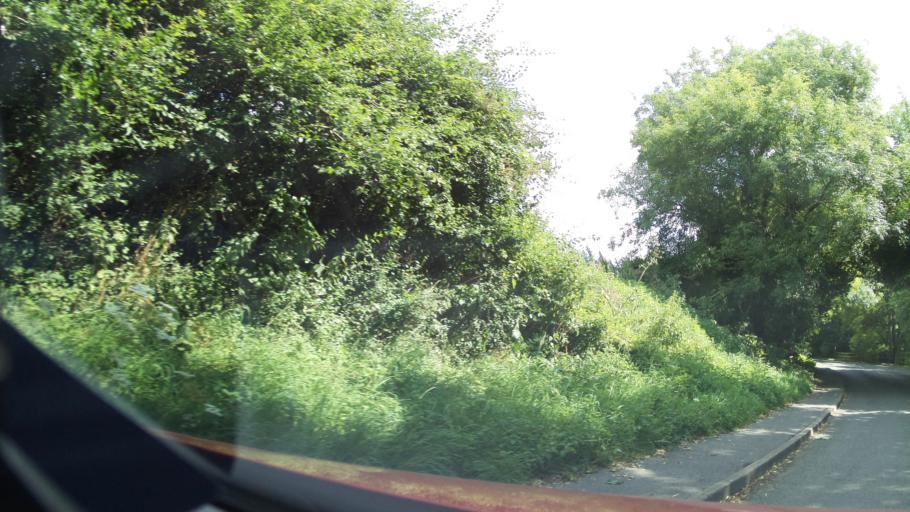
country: GB
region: England
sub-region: Borough of Swindon
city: Bishopstone
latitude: 51.5667
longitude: -1.6237
